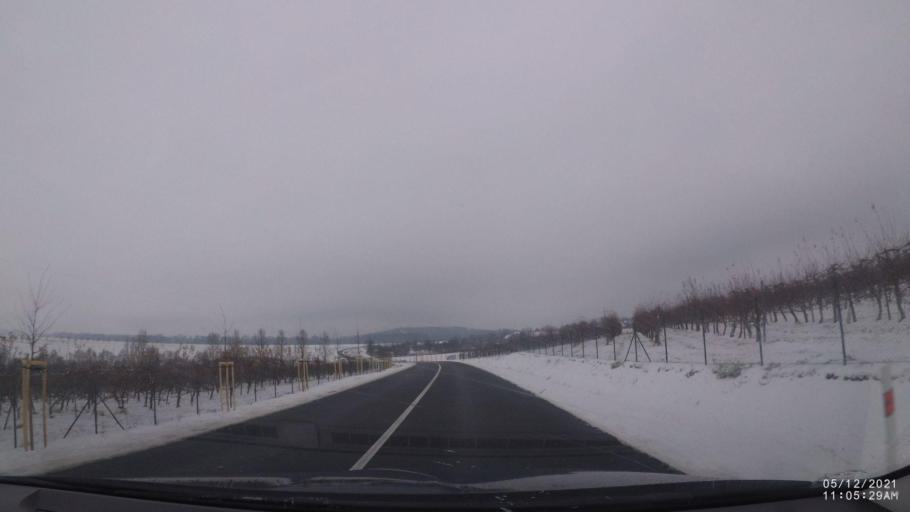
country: CZ
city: Solnice
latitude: 50.1744
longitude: 16.2222
